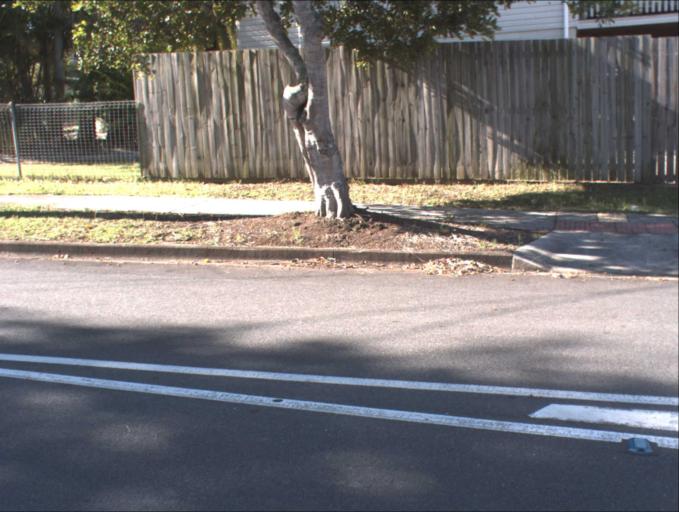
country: AU
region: Queensland
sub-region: Logan
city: Slacks Creek
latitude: -27.6514
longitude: 153.1325
